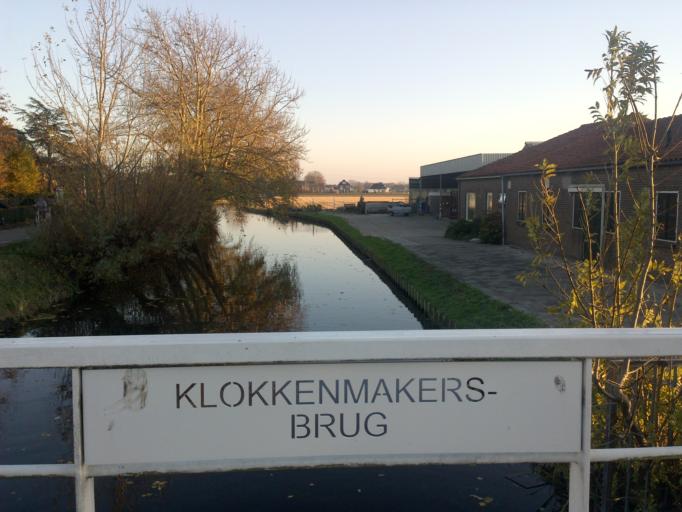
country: NL
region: South Holland
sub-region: Gemeente Teylingen
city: Voorhout
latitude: 52.2298
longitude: 4.5015
